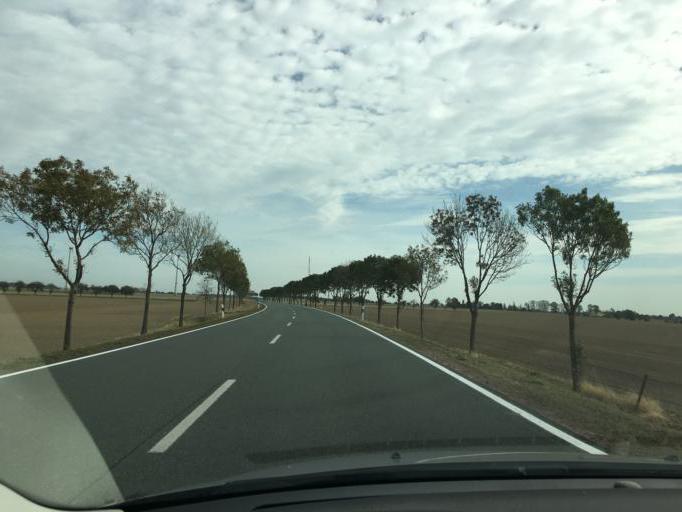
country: DE
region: Saxony
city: Stauchitz
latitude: 51.2794
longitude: 13.1798
